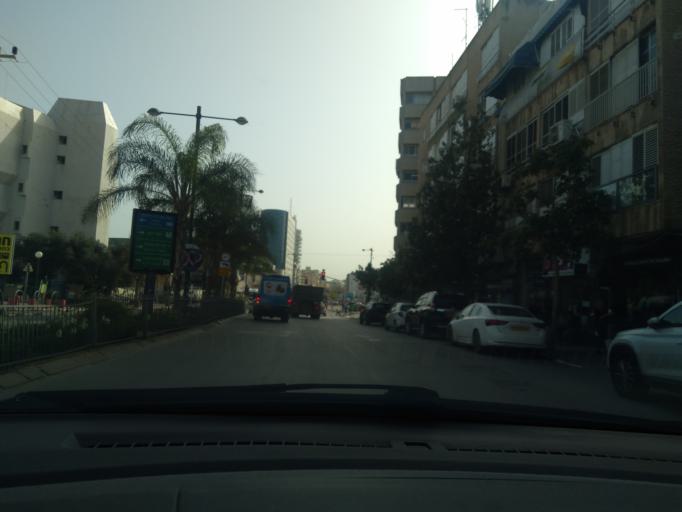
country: IL
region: Central District
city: Netanya
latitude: 32.3281
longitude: 34.8617
